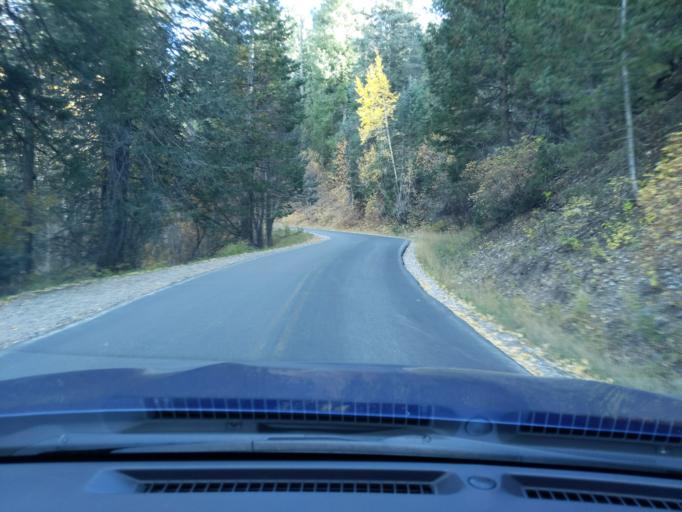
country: US
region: Arizona
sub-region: Pima County
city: Catalina
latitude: 32.4423
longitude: -110.7871
